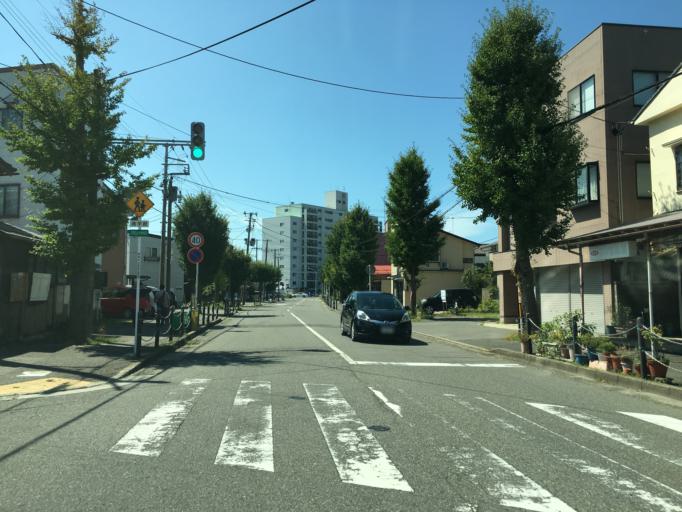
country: JP
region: Niigata
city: Niigata-shi
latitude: 37.9310
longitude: 139.0515
